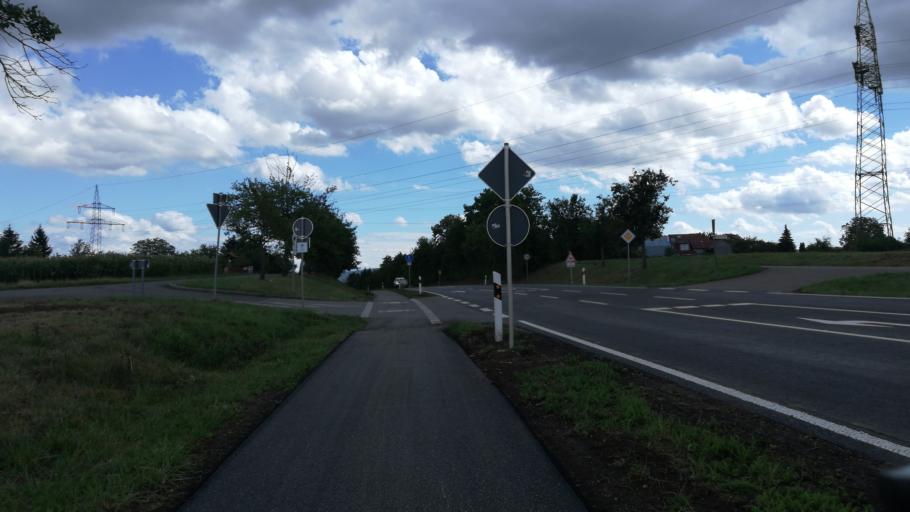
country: DE
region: Baden-Wuerttemberg
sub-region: Regierungsbezirk Stuttgart
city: Waiblingen
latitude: 48.8469
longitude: 9.3019
